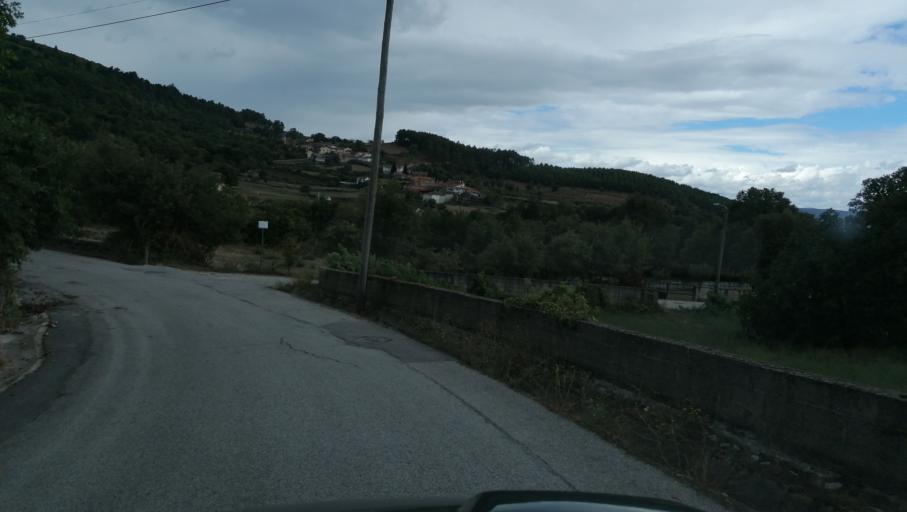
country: PT
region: Vila Real
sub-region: Vila Pouca de Aguiar
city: Vila Pouca de Aguiar
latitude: 41.5603
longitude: -7.6474
